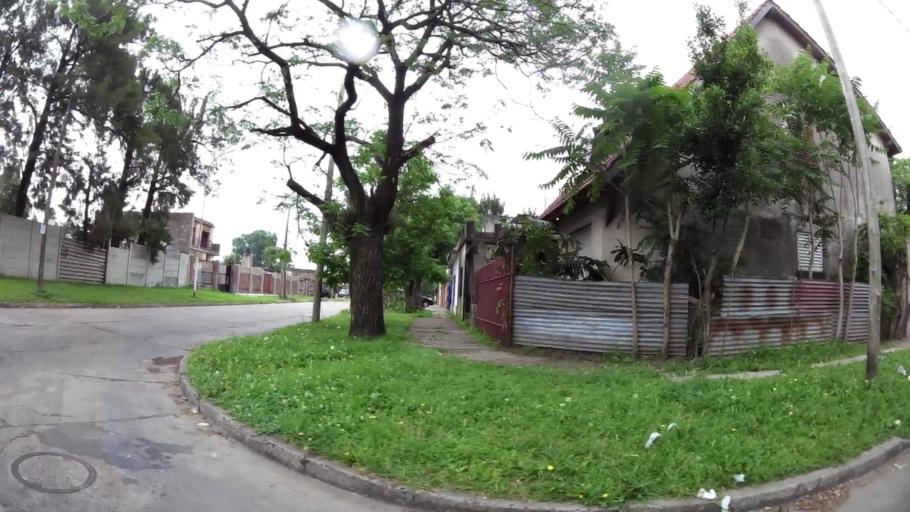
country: AR
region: Buenos Aires
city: San Justo
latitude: -34.7087
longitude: -58.5250
